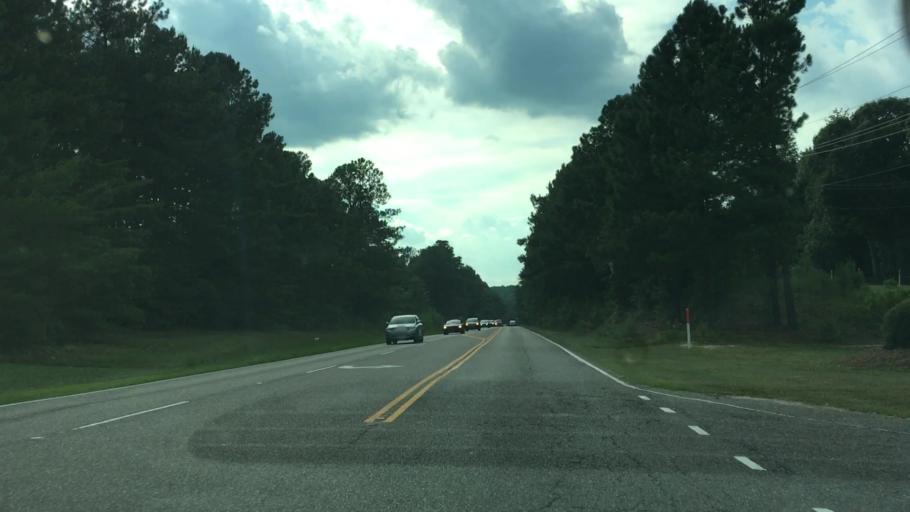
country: US
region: South Carolina
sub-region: Aiken County
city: Aiken
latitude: 33.5250
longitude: -81.7344
